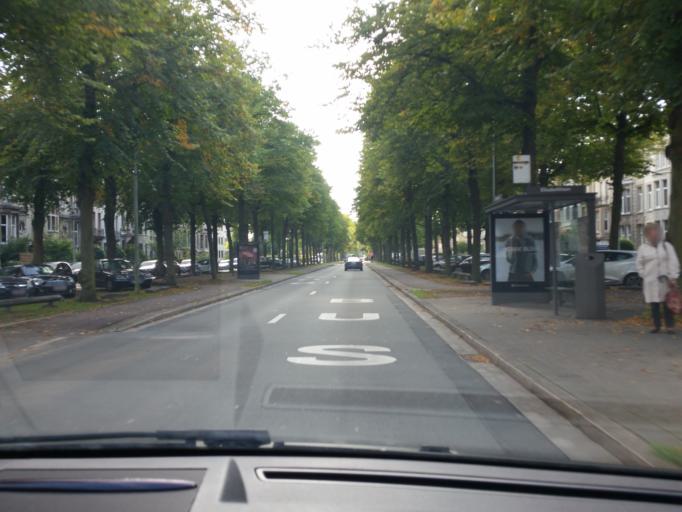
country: BE
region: Flanders
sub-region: Provincie Antwerpen
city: Mortsel
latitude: 51.1880
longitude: 4.4229
